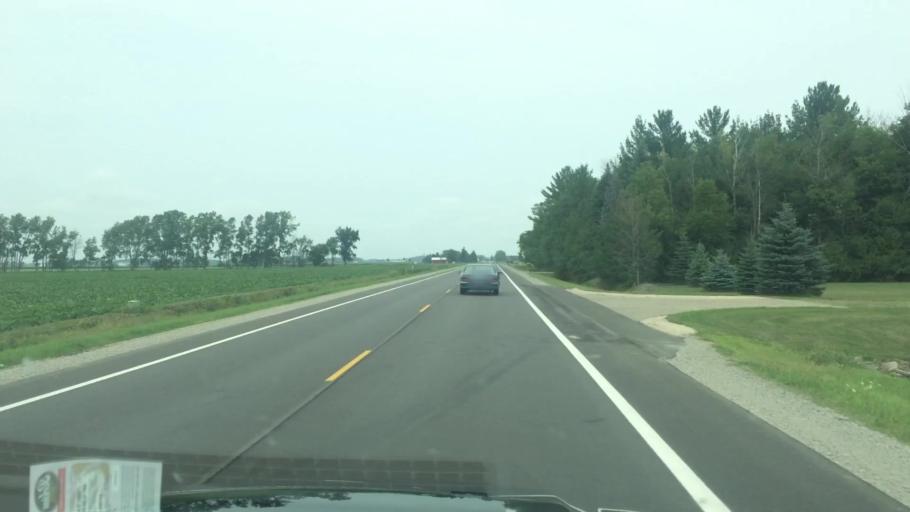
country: US
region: Michigan
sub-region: Huron County
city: Bad Axe
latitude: 43.9864
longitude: -83.0071
